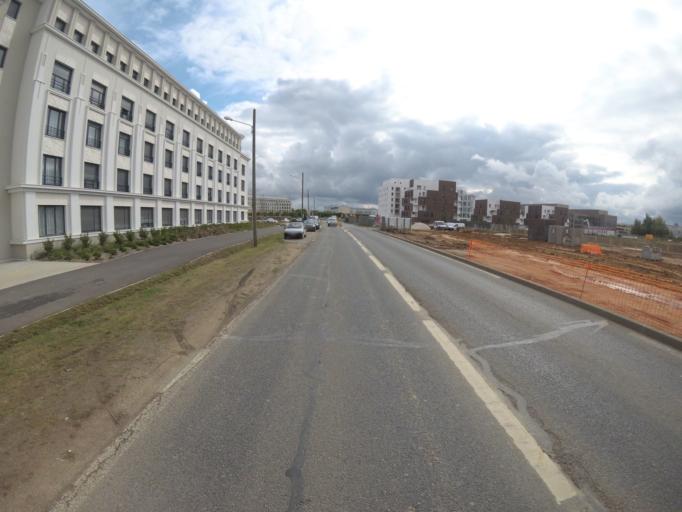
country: FR
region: Ile-de-France
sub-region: Departement de Seine-et-Marne
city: Serris
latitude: 48.8579
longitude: 2.7681
